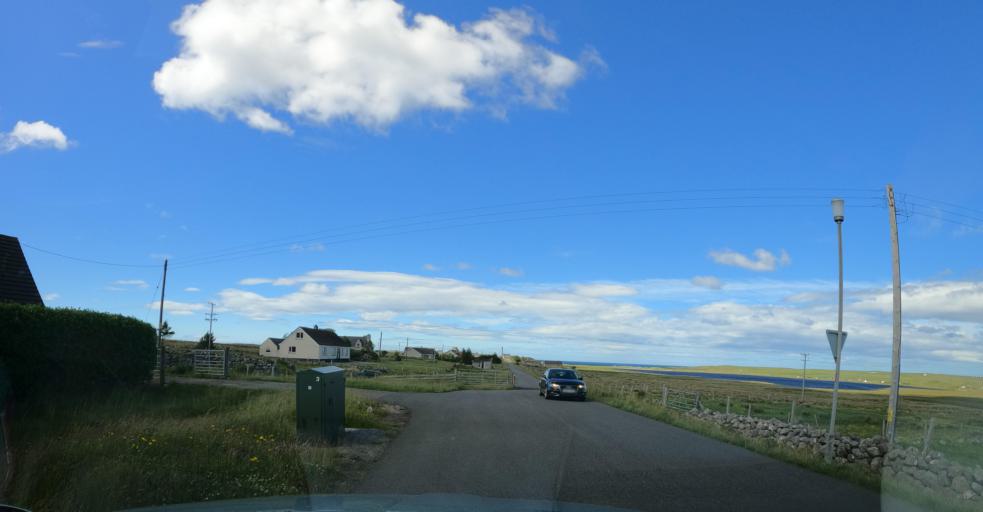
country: GB
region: Scotland
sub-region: Eilean Siar
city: Isle of Lewis
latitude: 58.3480
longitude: -6.5446
